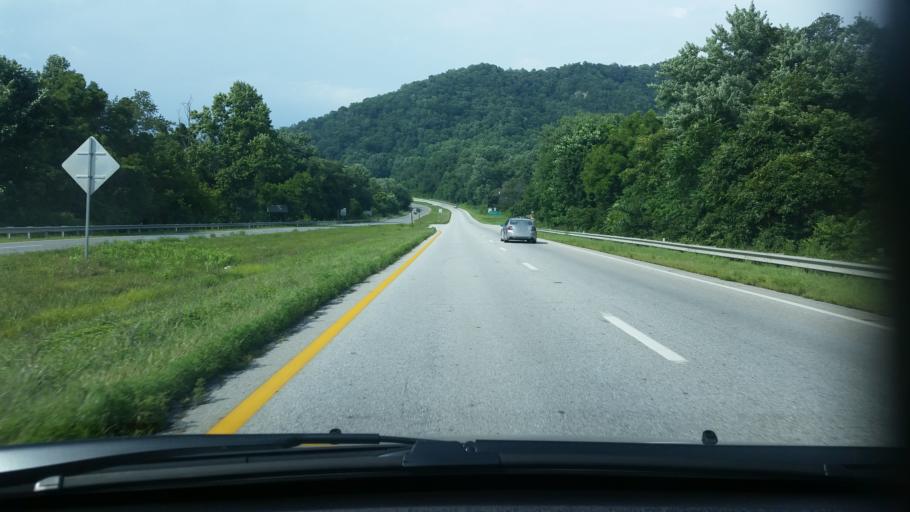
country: US
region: Virginia
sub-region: Nelson County
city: Lovingston
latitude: 37.7628
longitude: -78.8722
